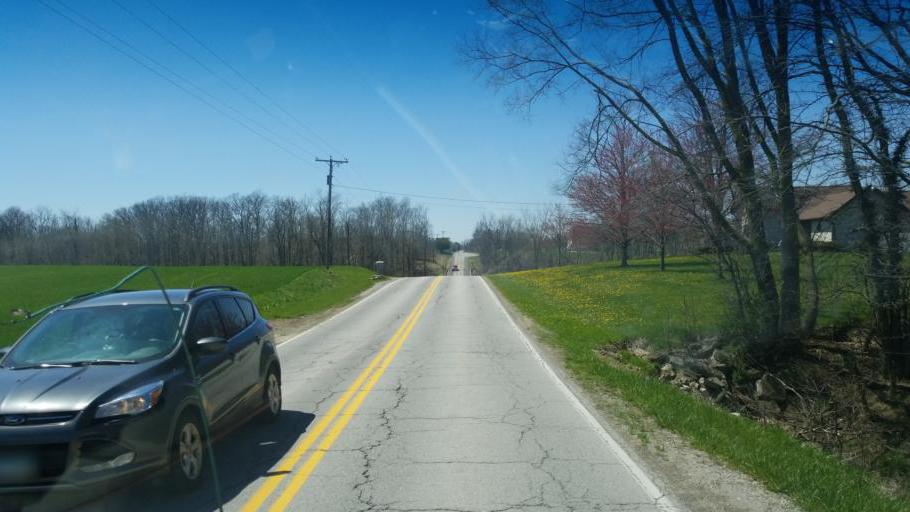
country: US
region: Ohio
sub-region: Huron County
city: Willard
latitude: 41.0688
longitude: -82.7213
